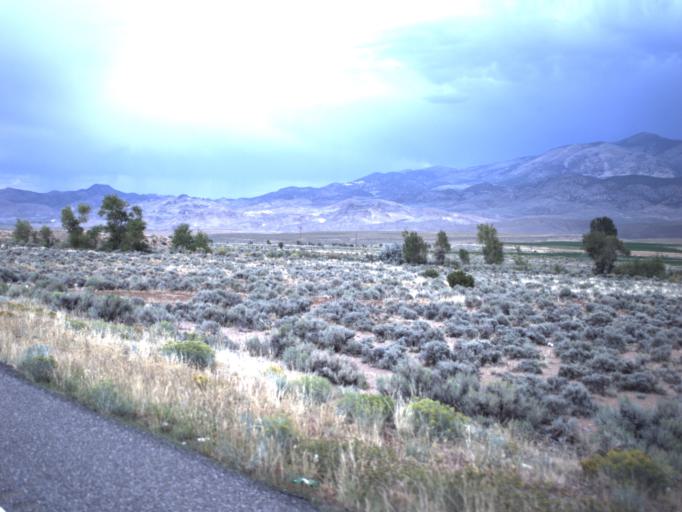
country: US
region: Utah
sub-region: Piute County
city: Junction
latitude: 38.3817
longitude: -112.2284
